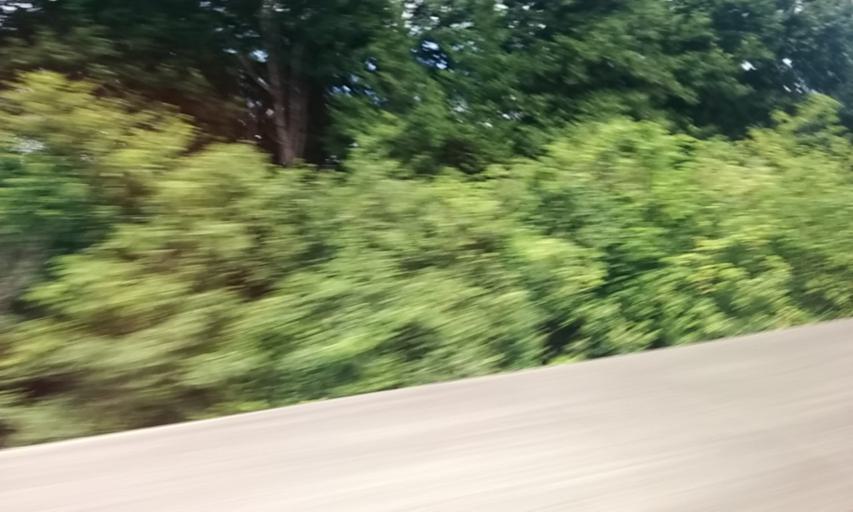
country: JP
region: Tochigi
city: Yaita
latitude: 36.7882
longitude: 139.9537
